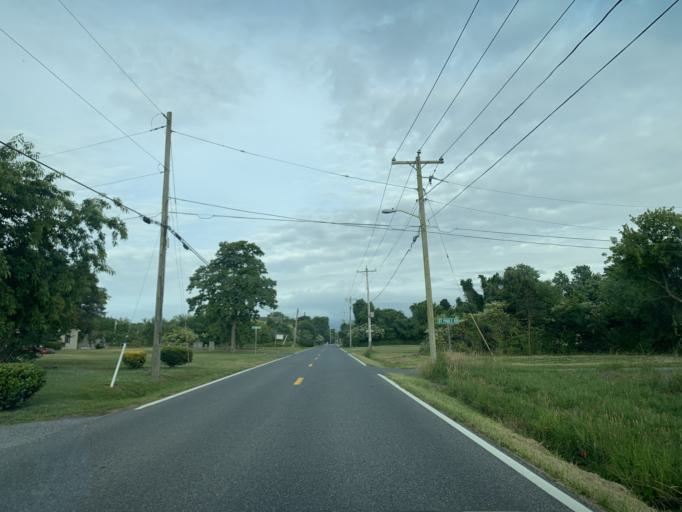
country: US
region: Virginia
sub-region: Accomack County
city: Captains Cove
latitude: 38.0563
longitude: -75.4161
